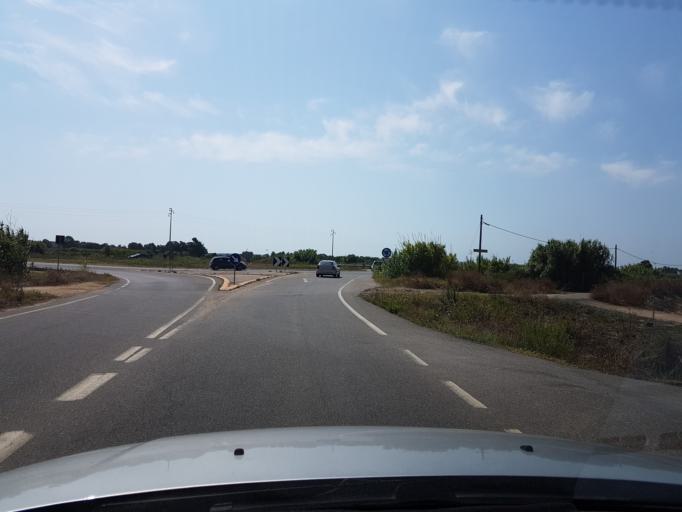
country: IT
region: Sardinia
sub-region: Provincia di Oristano
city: Cabras
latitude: 39.9194
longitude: 8.5385
